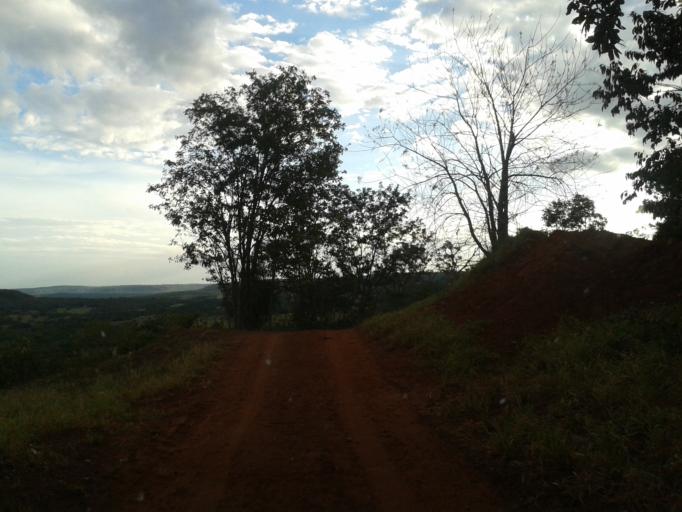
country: BR
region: Minas Gerais
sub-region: Campina Verde
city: Campina Verde
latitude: -19.3491
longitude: -49.6632
